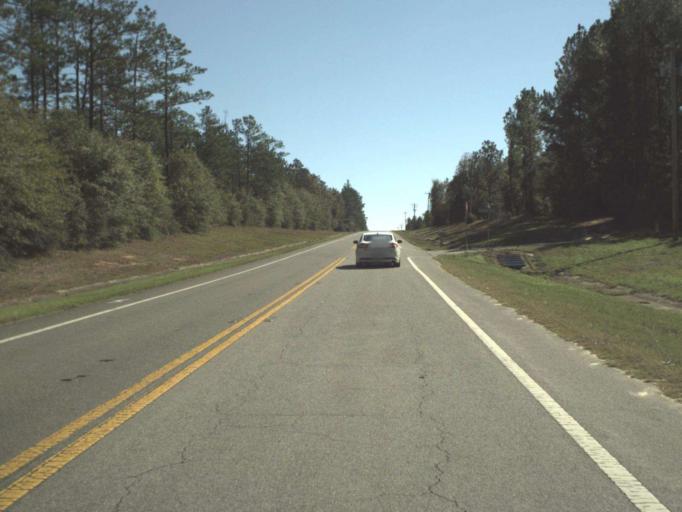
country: US
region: Florida
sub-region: Okaloosa County
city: Crestview
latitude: 30.8313
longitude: -86.7313
